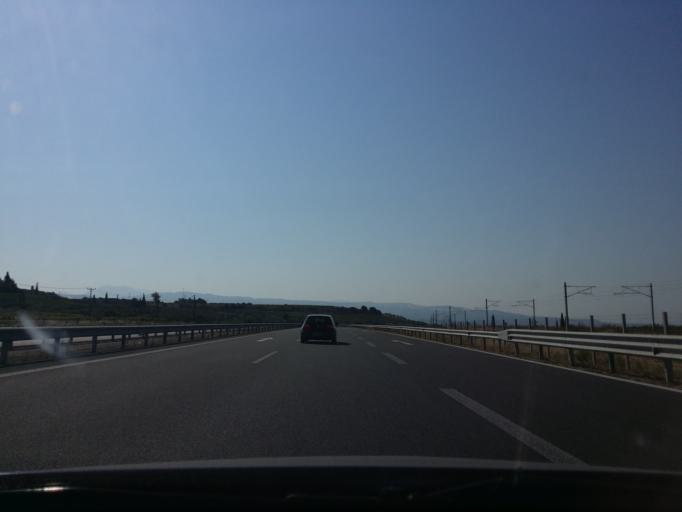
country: GR
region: Peloponnese
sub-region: Nomos Korinthias
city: Lekhaio
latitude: 37.9119
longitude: 22.8362
